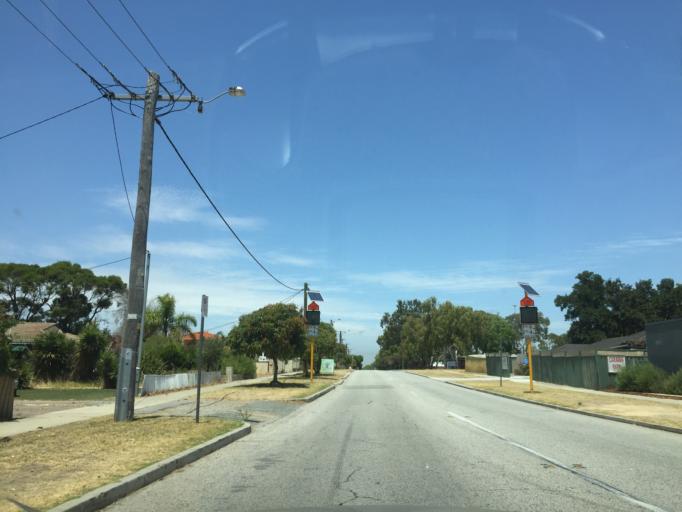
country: AU
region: Western Australia
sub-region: Canning
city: Queens Park
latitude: -31.9973
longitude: 115.9470
